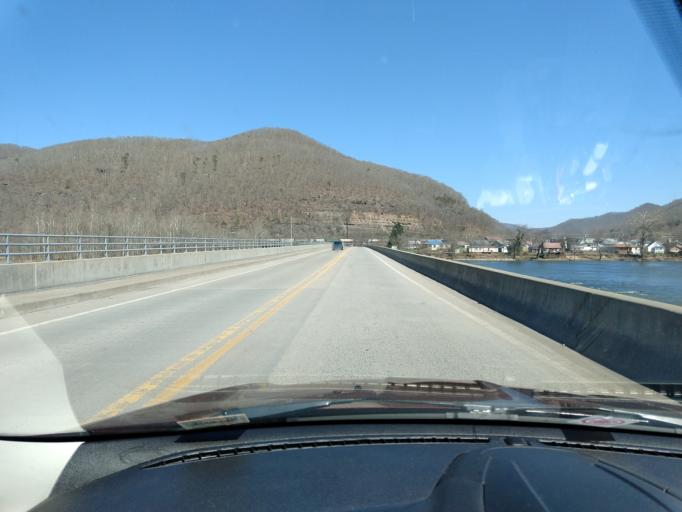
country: US
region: West Virginia
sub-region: Summers County
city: Hinton
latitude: 37.6505
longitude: -80.8882
